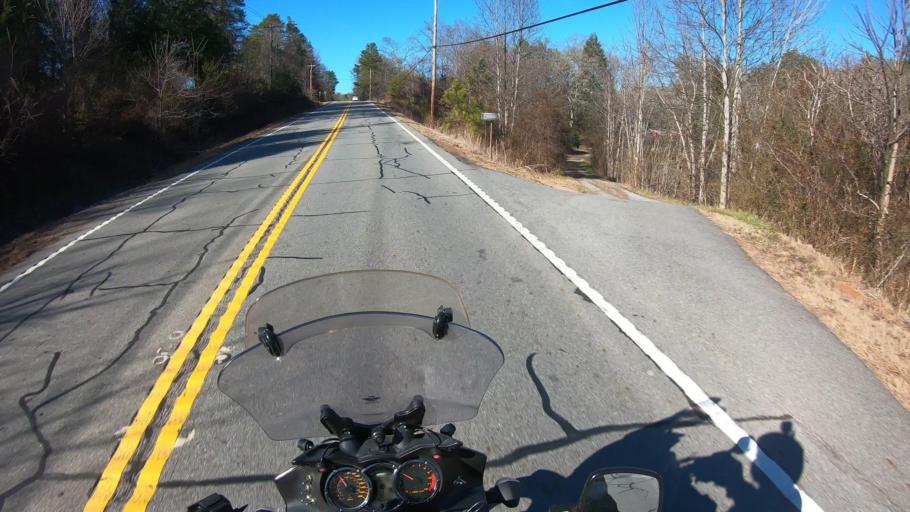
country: US
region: Georgia
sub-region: Fannin County
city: McCaysville
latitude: 34.9412
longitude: -84.3147
